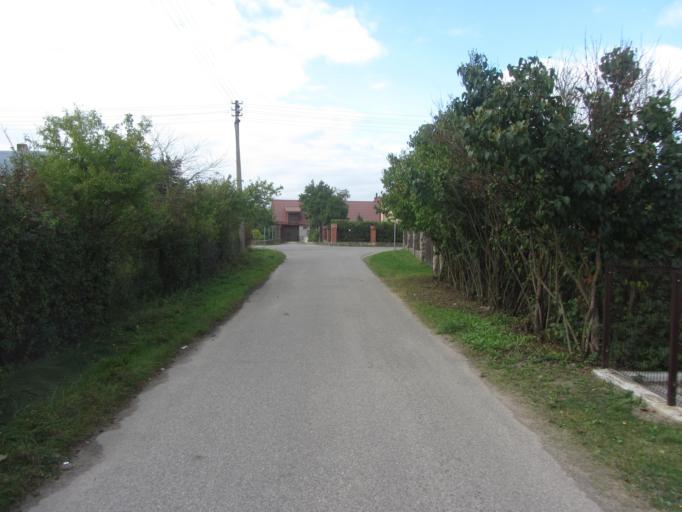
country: LT
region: Vilnius County
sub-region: Trakai
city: Rudiskes
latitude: 54.5194
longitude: 24.8268
